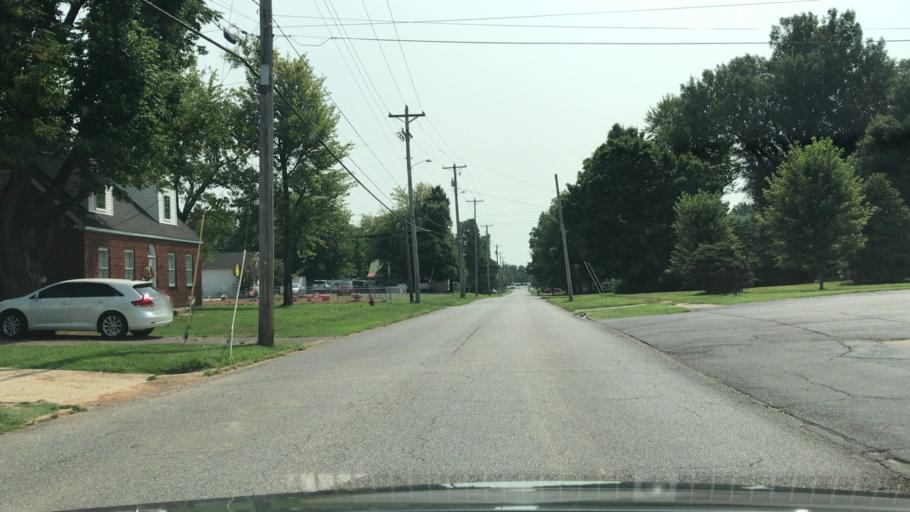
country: US
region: Kentucky
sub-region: Graves County
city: Mayfield
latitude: 36.7297
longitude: -88.6372
